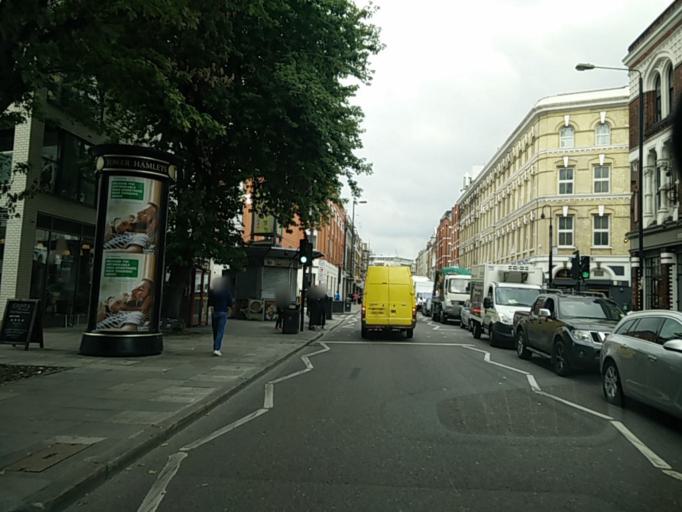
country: GB
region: England
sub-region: Greater London
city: Bethnal Green
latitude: 51.5167
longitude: -0.0729
